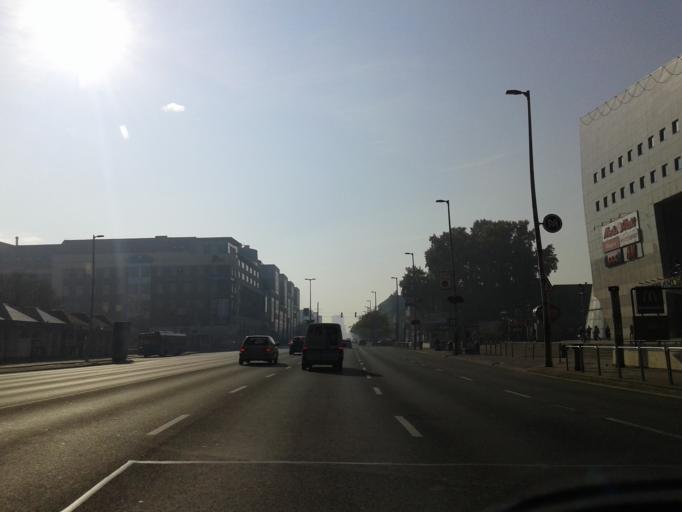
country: HU
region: Budapest
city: Budapest IV. keruelet
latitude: 47.5496
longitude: 19.0734
